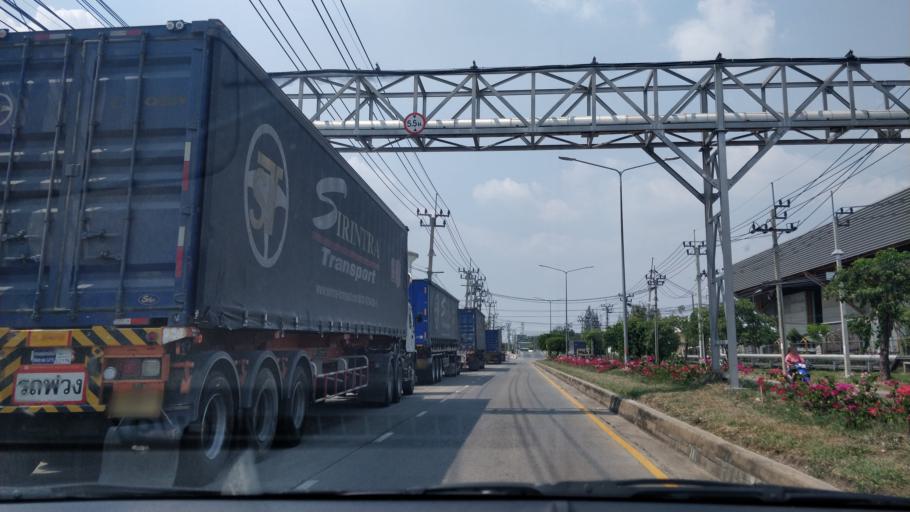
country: TH
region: Bangkok
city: Lat Krabang
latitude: 13.7660
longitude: 100.7833
